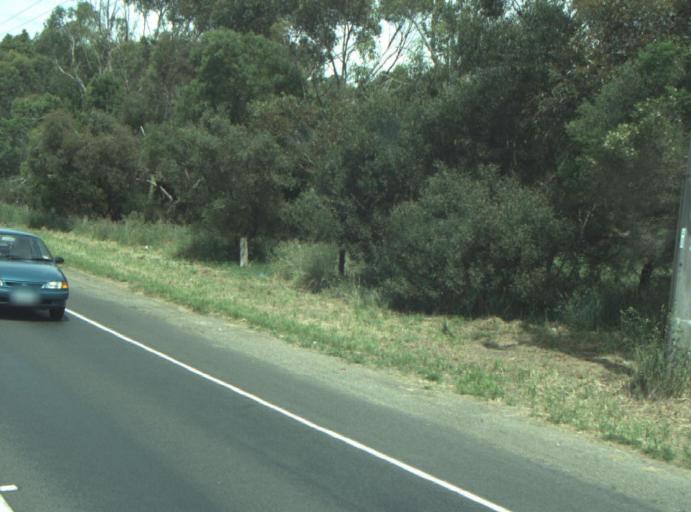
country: AU
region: Victoria
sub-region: Greater Geelong
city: Clifton Springs
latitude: -38.1579
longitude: 144.5858
